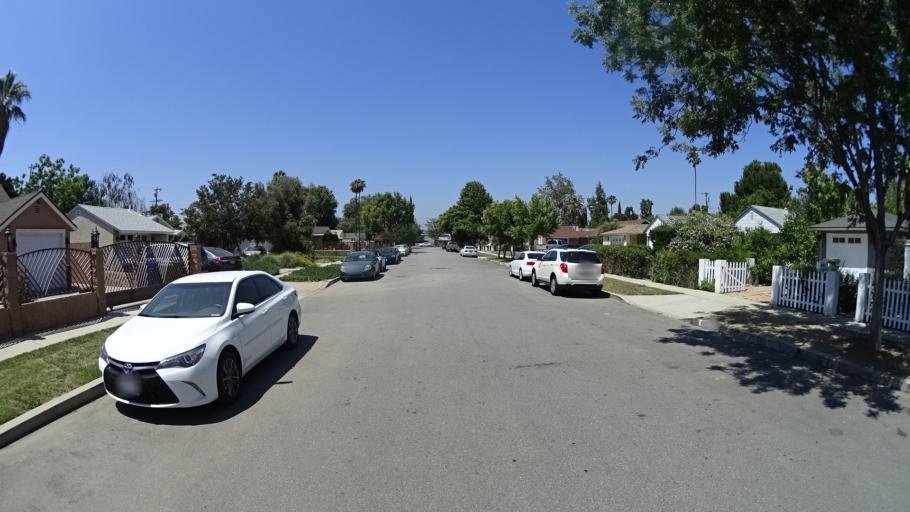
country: US
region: California
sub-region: Los Angeles County
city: Van Nuys
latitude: 34.1919
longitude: -118.4346
